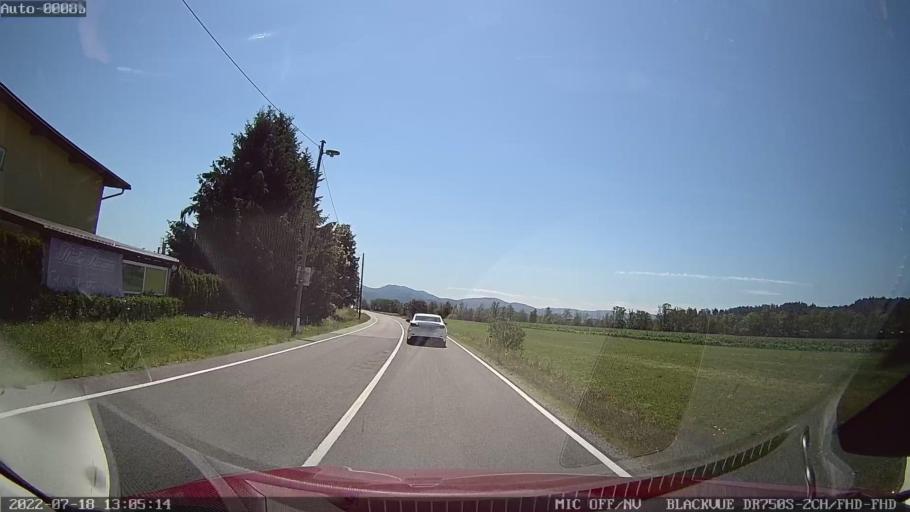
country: SI
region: Brezovica
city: Vnanje Gorice
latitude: 46.0382
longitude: 14.4430
